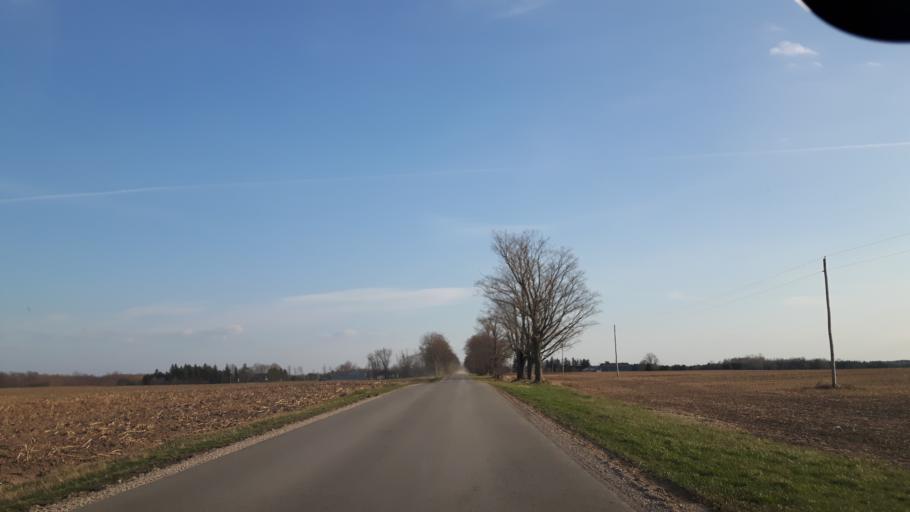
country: CA
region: Ontario
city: Goderich
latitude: 43.6308
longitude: -81.6643
